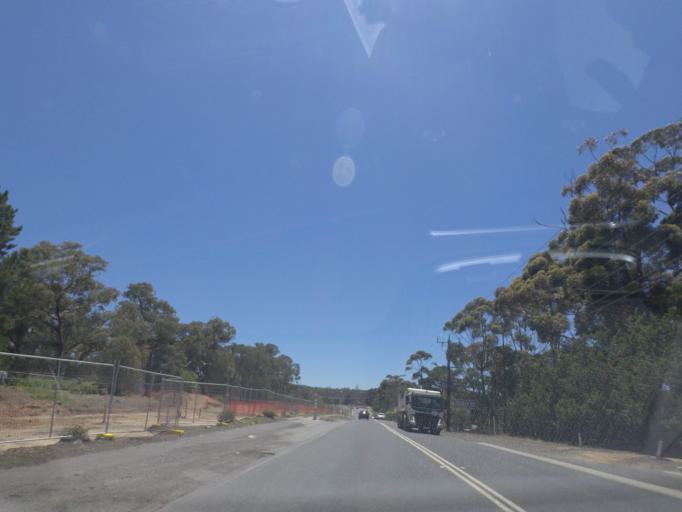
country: AU
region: Victoria
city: Plenty
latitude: -37.6617
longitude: 145.1242
